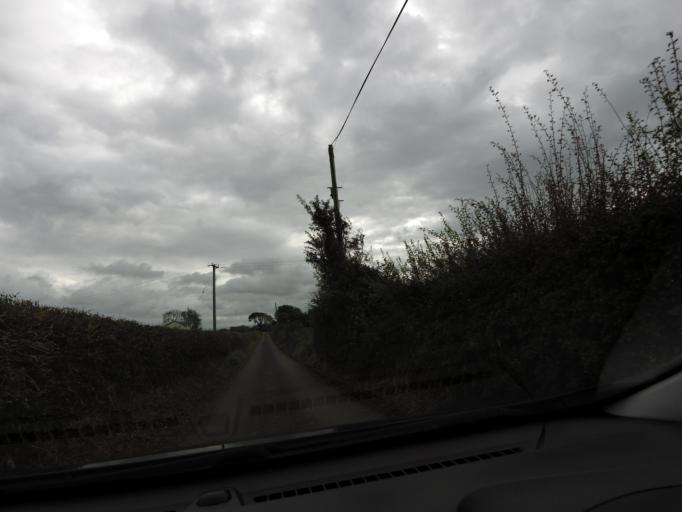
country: IE
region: Connaught
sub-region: County Galway
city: Athenry
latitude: 53.2990
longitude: -8.6829
